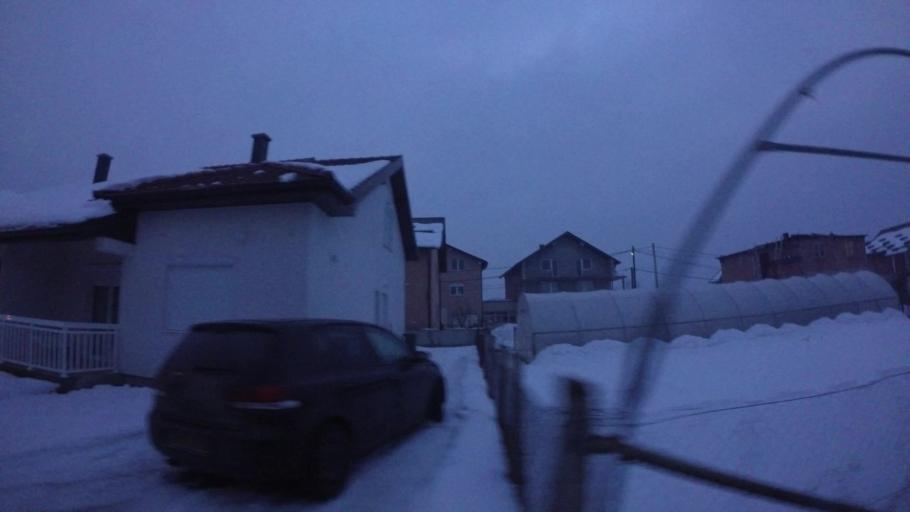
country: BA
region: Federation of Bosnia and Herzegovina
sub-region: Kanton Sarajevo
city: Sarajevo
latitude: 43.8546
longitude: 18.2914
